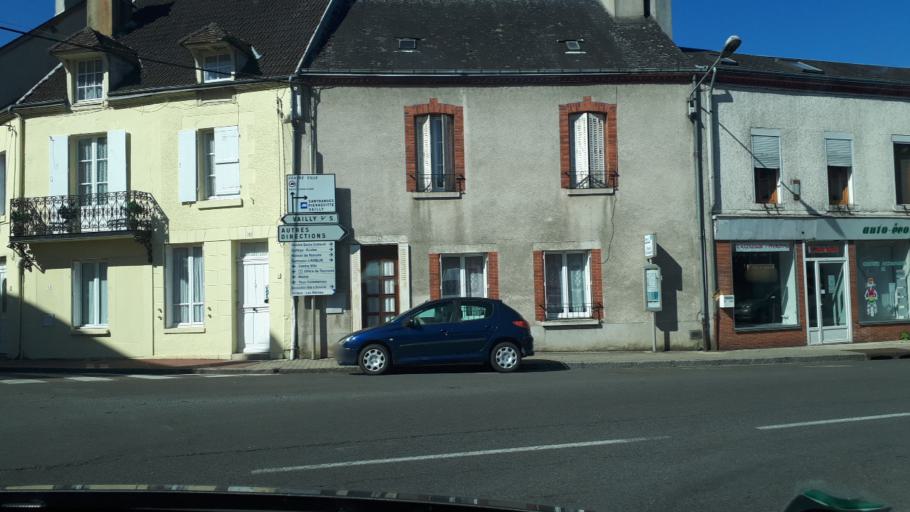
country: FR
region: Centre
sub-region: Departement du Loiret
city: Briare
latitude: 47.5922
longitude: 2.7538
